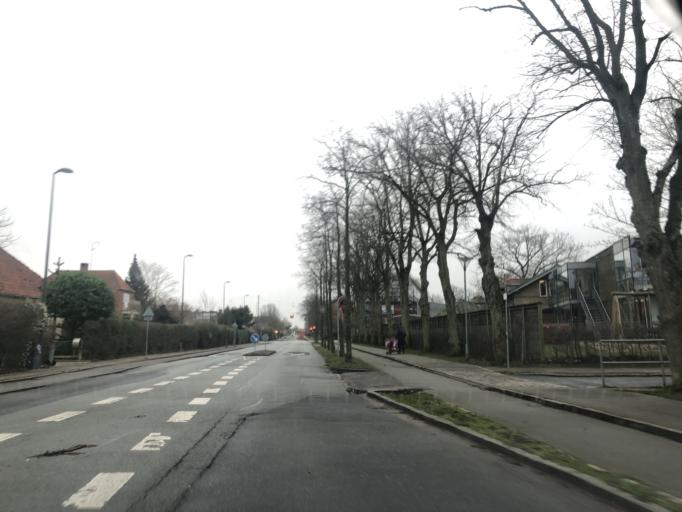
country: DK
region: Capital Region
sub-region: Tarnby Kommune
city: Tarnby
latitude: 55.6473
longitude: 12.6050
